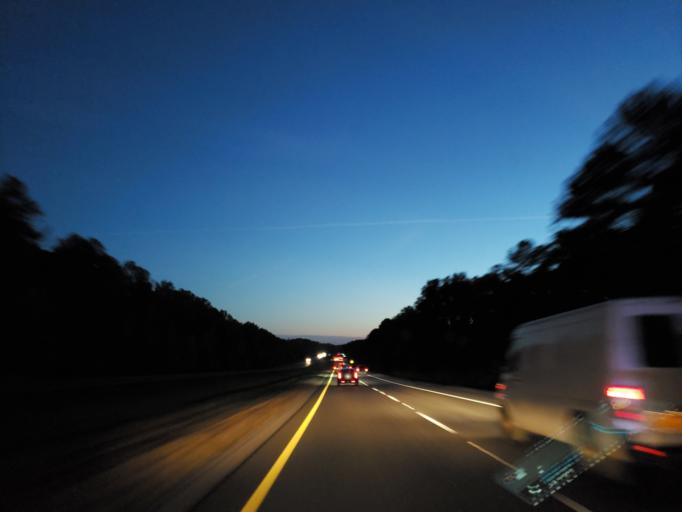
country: US
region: Mississippi
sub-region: Clarke County
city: Stonewall
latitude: 32.2335
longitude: -88.8320
